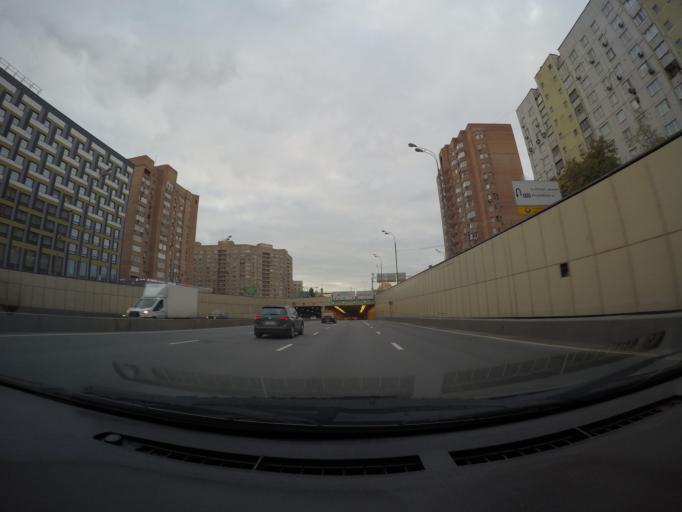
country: RU
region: Moscow
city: Lefortovo
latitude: 55.7762
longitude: 37.6817
